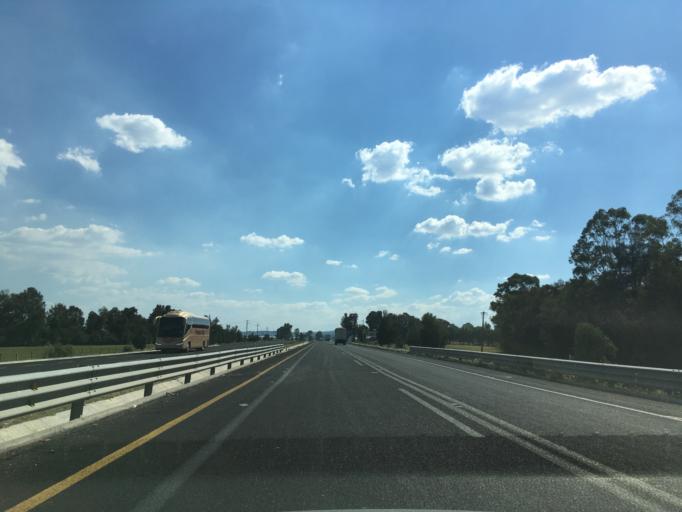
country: MX
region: Mexico
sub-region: Jilotepec
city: Xhixhata
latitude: 19.9819
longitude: -99.5127
